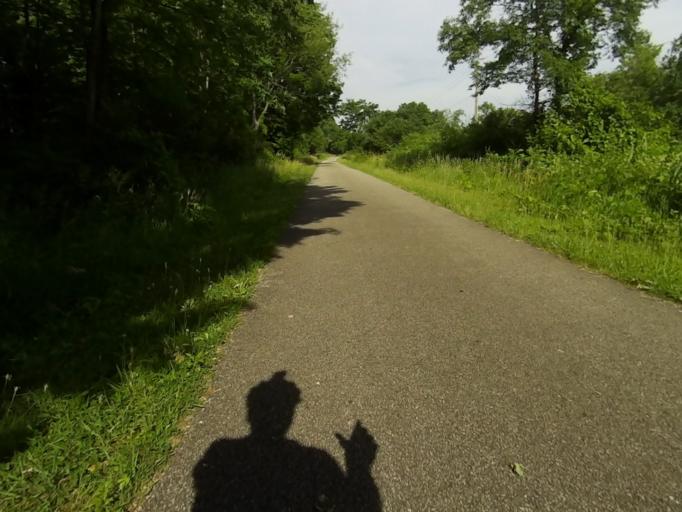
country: US
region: Ohio
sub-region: Summit County
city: Stow
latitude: 41.1933
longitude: -81.4155
